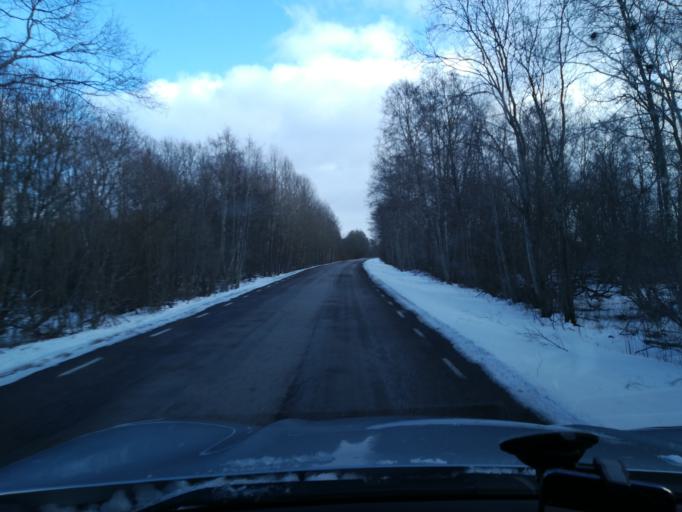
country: EE
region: Harju
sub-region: Keila linn
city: Keila
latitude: 59.4407
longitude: 24.3921
